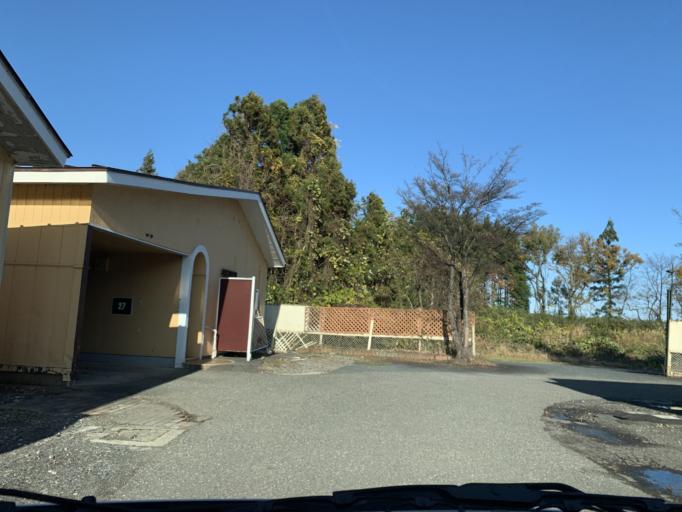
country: JP
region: Iwate
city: Kitakami
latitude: 39.2328
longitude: 141.0815
